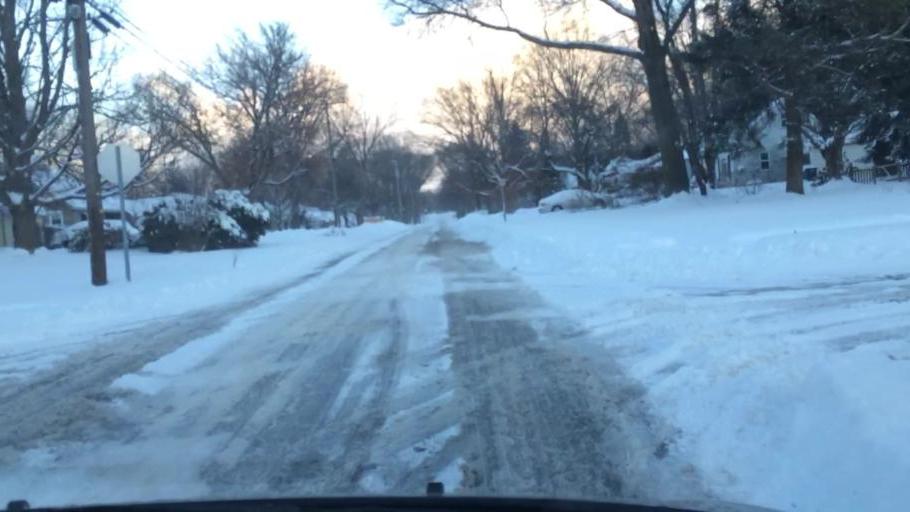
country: US
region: Ohio
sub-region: Portage County
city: Kent
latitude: 41.1404
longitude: -81.3549
